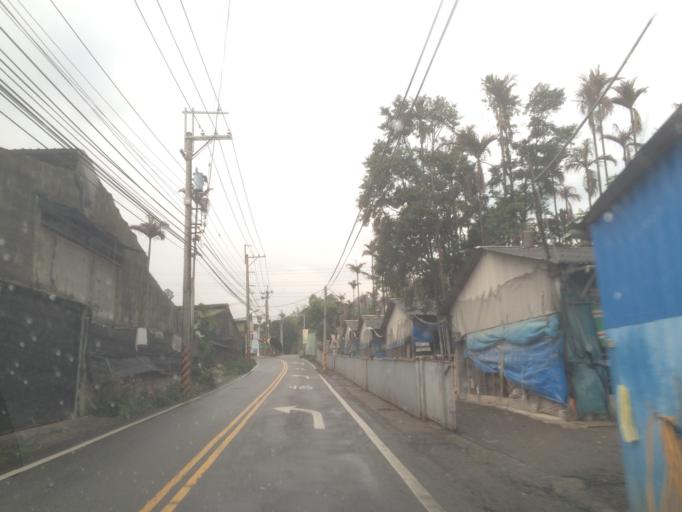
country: TW
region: Taiwan
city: Fengyuan
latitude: 24.1782
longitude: 120.8208
